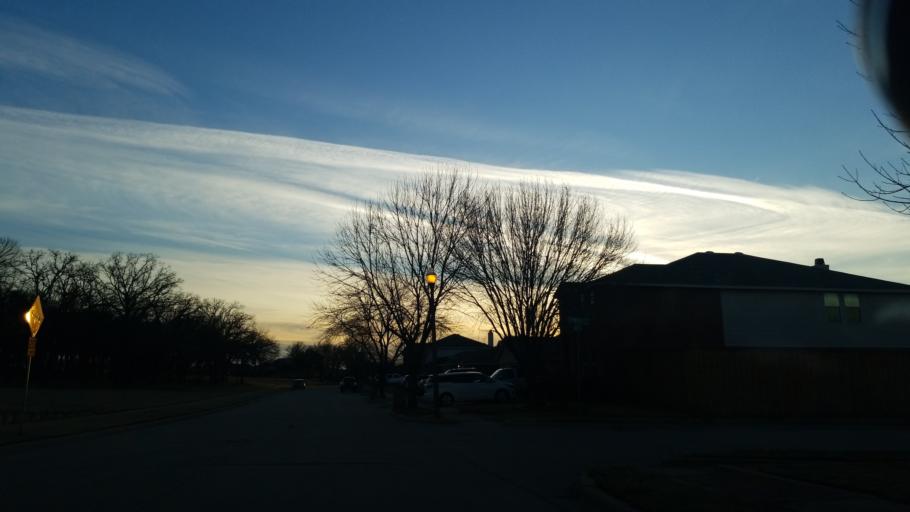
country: US
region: Texas
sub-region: Denton County
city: Corinth
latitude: 33.1565
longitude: -97.1007
